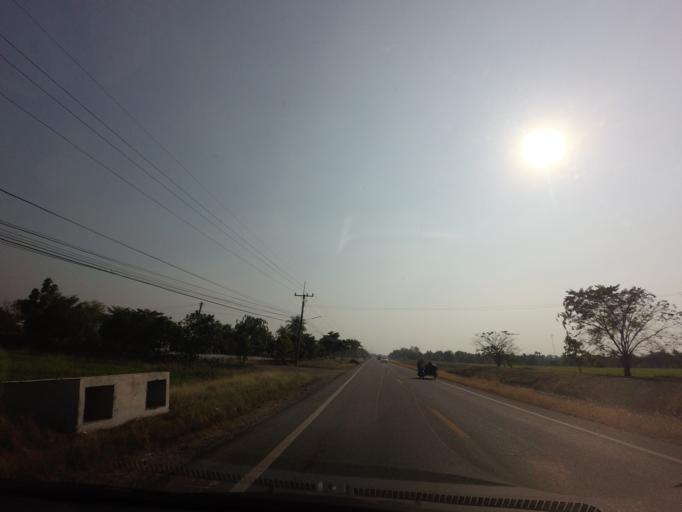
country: TH
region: Chachoengsao
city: Khlong Khuean
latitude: 13.7761
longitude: 101.1724
